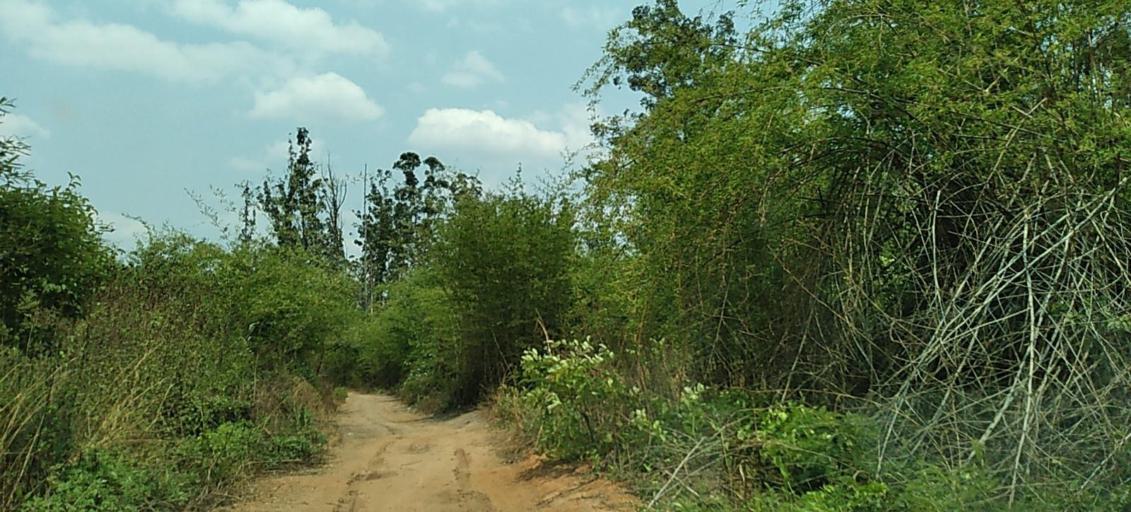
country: ZM
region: Copperbelt
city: Kalulushi
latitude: -12.7582
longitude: 28.0276
